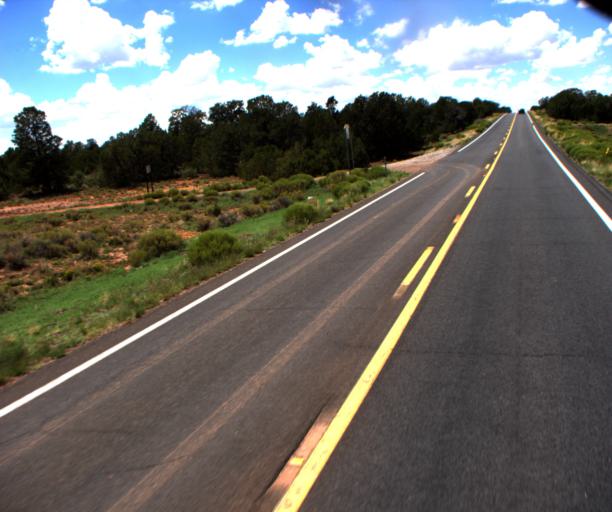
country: US
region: Arizona
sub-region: Coconino County
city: Parks
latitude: 35.5948
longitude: -112.0041
